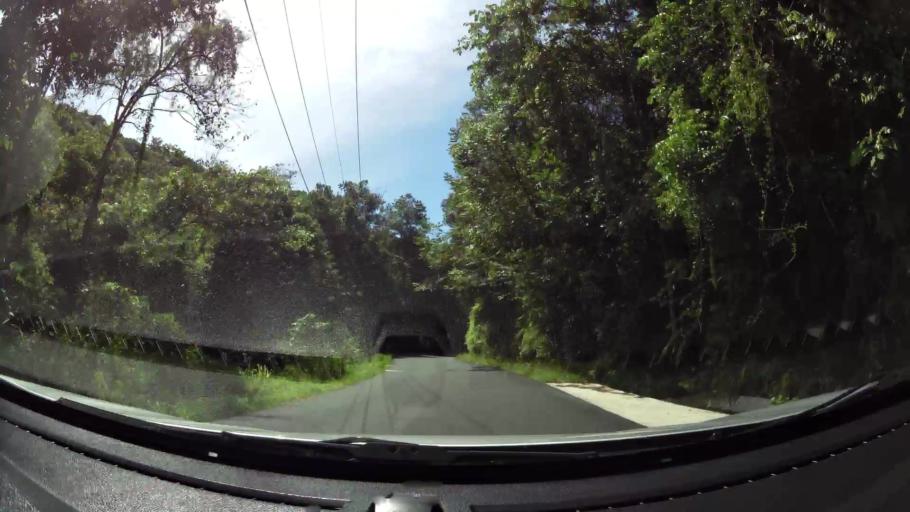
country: CR
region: San Jose
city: San Isidro
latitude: 9.2806
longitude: -83.8242
